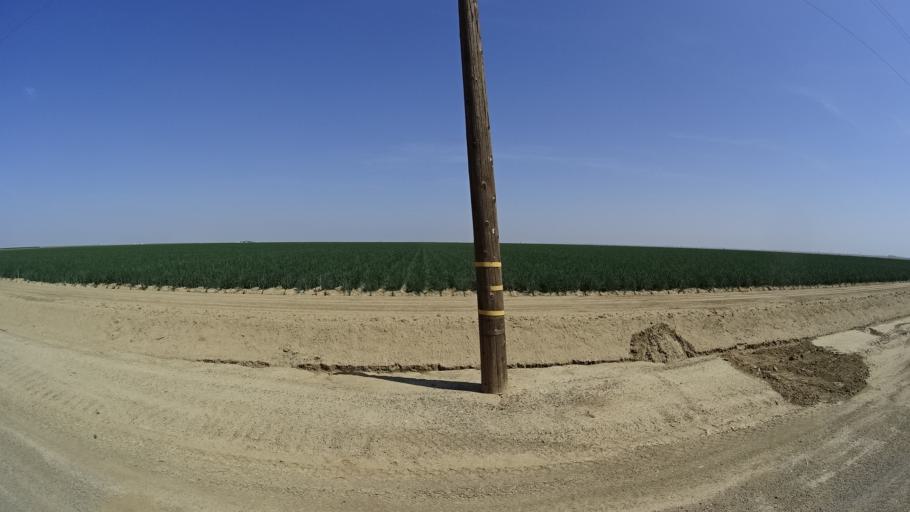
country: US
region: California
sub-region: Kings County
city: Kettleman City
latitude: 36.0942
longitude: -119.9627
